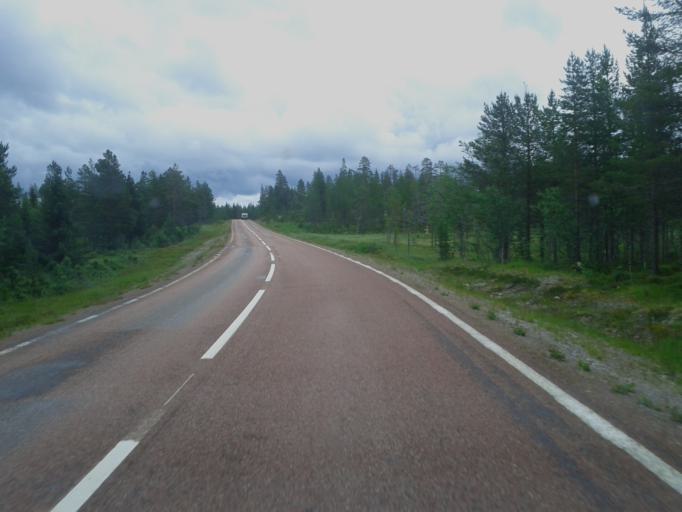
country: NO
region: Hedmark
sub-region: Engerdal
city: Engerdal
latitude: 61.8039
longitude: 12.3849
